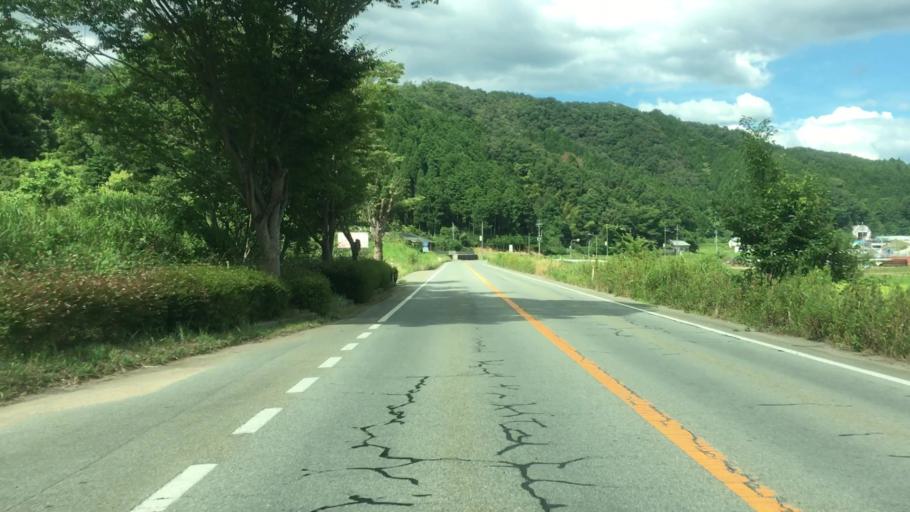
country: JP
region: Hyogo
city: Toyooka
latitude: 35.4669
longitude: 134.7568
